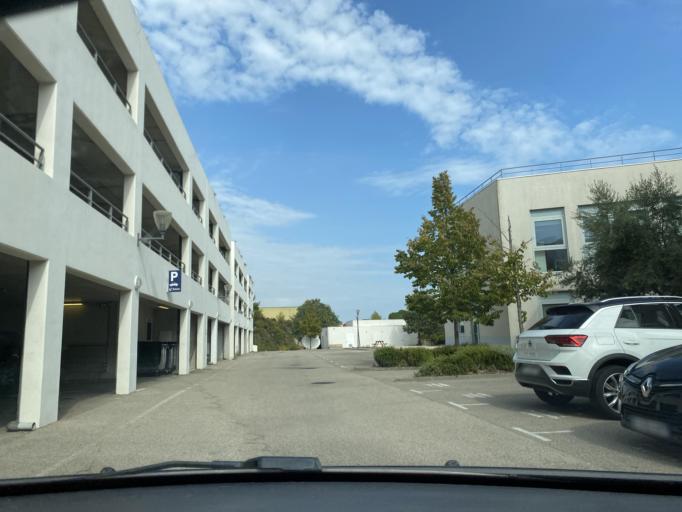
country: FR
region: Provence-Alpes-Cote d'Azur
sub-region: Departement des Alpes-Maritimes
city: Biot
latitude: 43.6274
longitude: 7.0478
